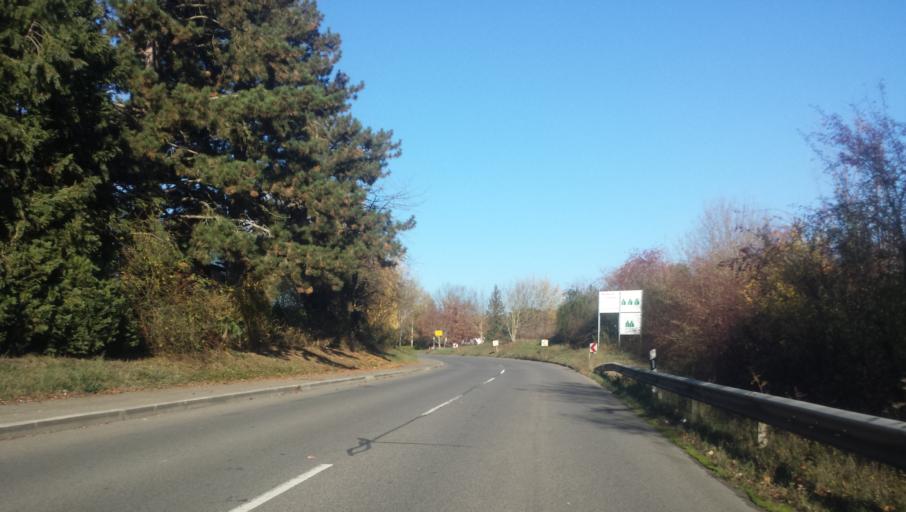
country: DE
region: Baden-Wuerttemberg
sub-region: Karlsruhe Region
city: Obrigheim
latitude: 49.3355
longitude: 9.1062
